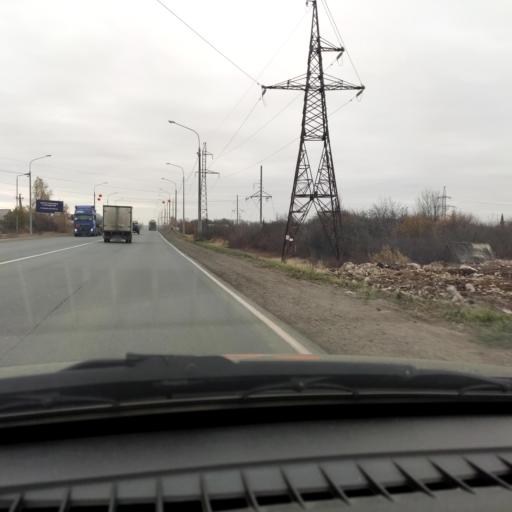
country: RU
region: Samara
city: Zhigulevsk
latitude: 53.3830
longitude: 49.4557
